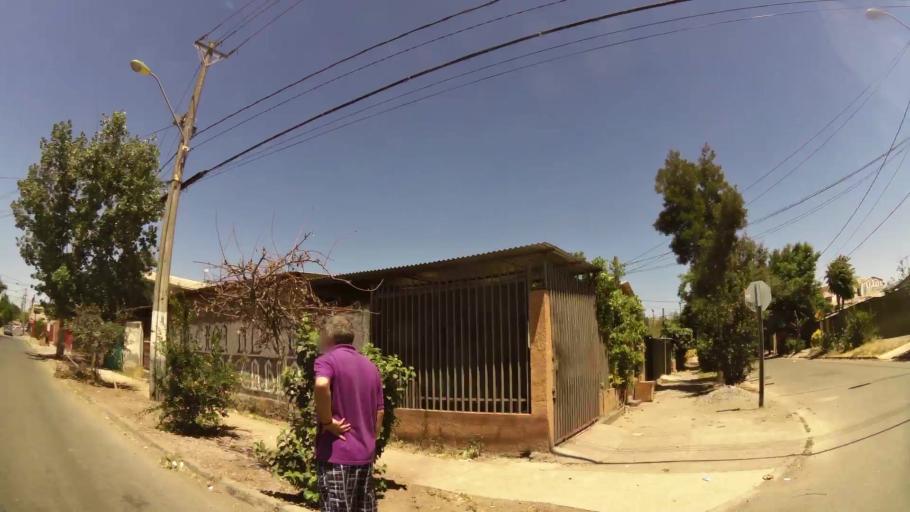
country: CL
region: Santiago Metropolitan
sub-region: Provincia de Santiago
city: La Pintana
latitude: -33.5704
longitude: -70.6615
